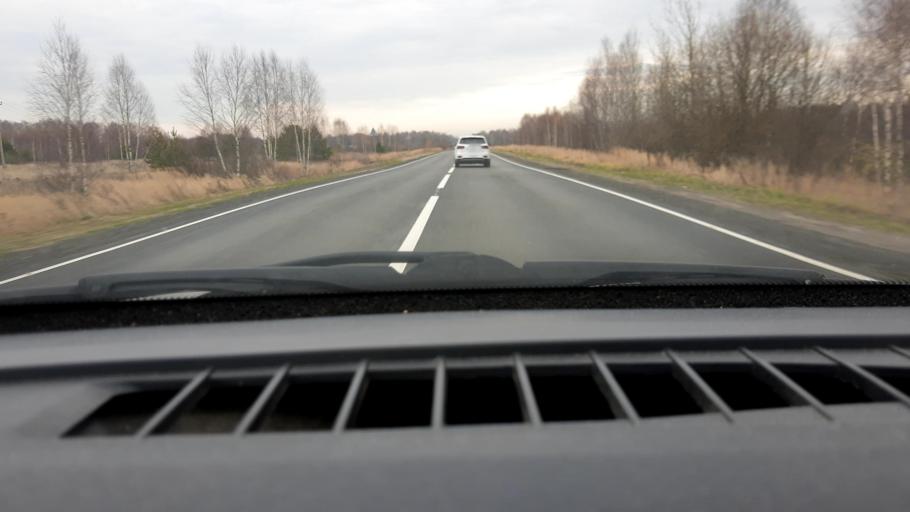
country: RU
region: Nizjnij Novgorod
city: Novaya Balakhna
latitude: 56.5870
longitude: 43.6711
